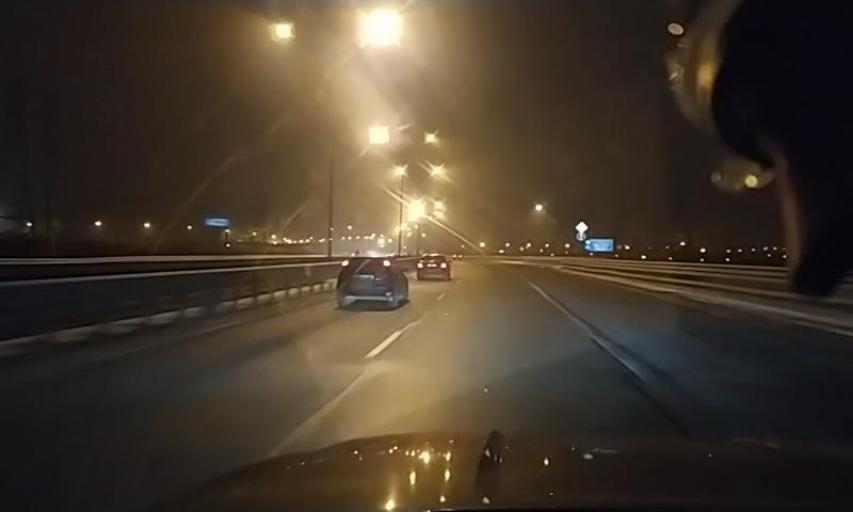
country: RU
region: Leningrad
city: Bugry
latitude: 60.0968
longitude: 30.3800
